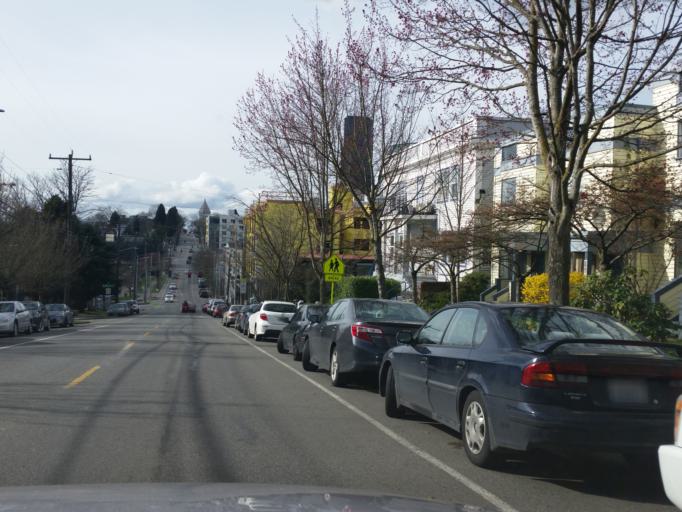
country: US
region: Washington
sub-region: King County
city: Seattle
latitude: 47.6018
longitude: -122.3119
